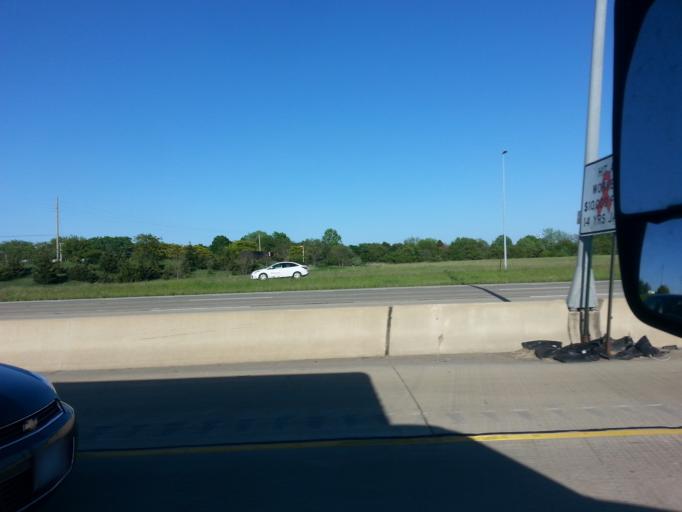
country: US
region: Illinois
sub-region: McLean County
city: Bloomington
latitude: 40.4870
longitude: -89.0286
